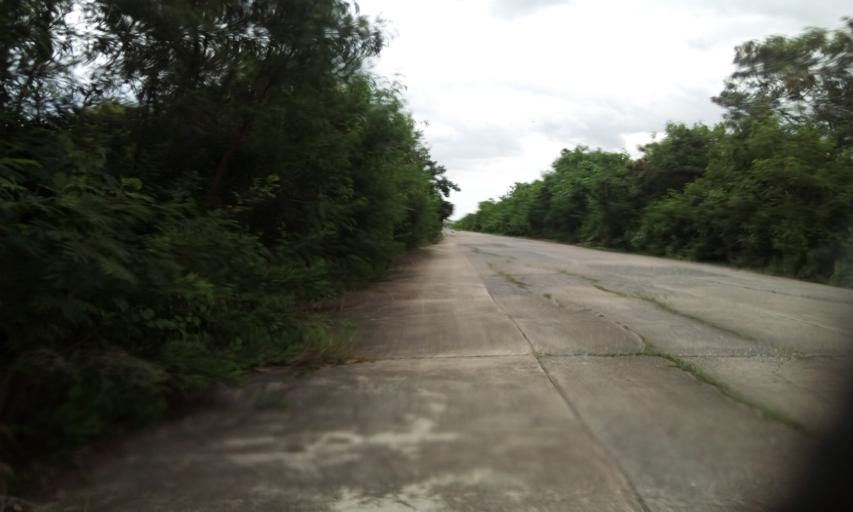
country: TH
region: Pathum Thani
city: Nong Suea
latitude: 14.0691
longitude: 100.8353
